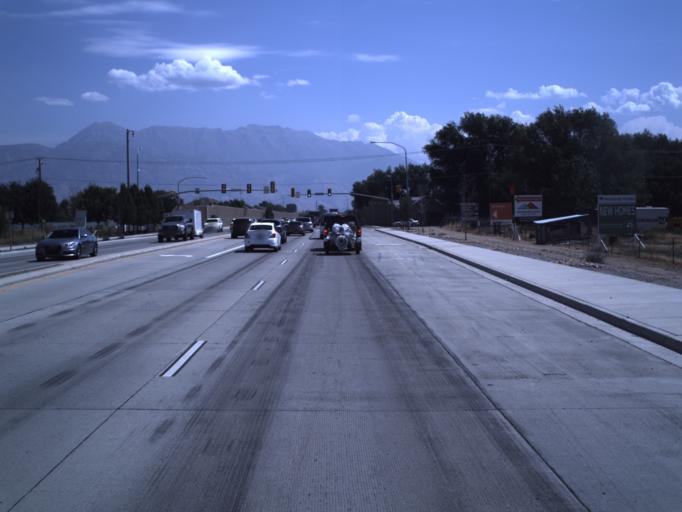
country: US
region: Utah
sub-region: Utah County
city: Saratoga Springs
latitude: 40.3761
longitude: -111.8883
